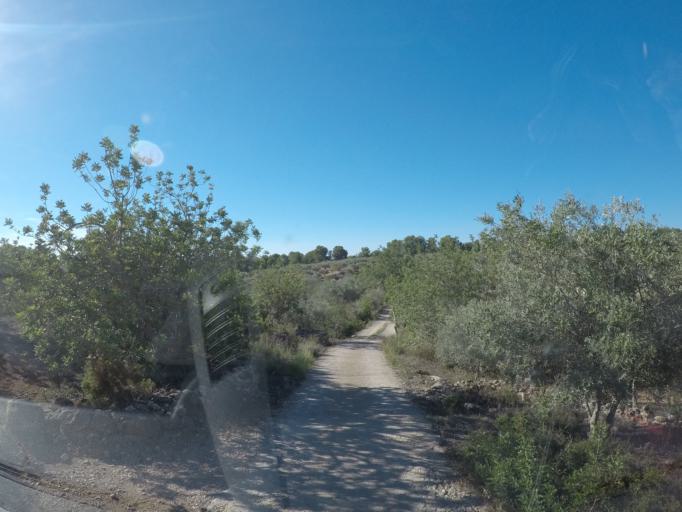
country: ES
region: Catalonia
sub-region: Provincia de Tarragona
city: El Perello
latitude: 40.9192
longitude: 0.7231
